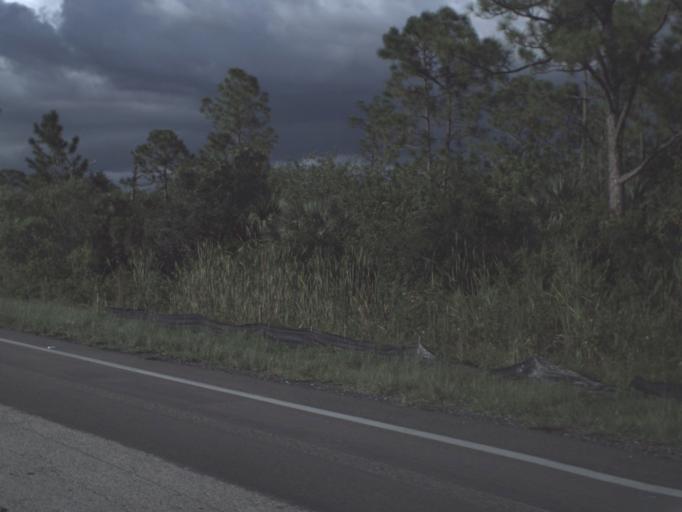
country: US
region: Florida
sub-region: Charlotte County
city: Harbour Heights
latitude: 27.0253
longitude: -82.0513
